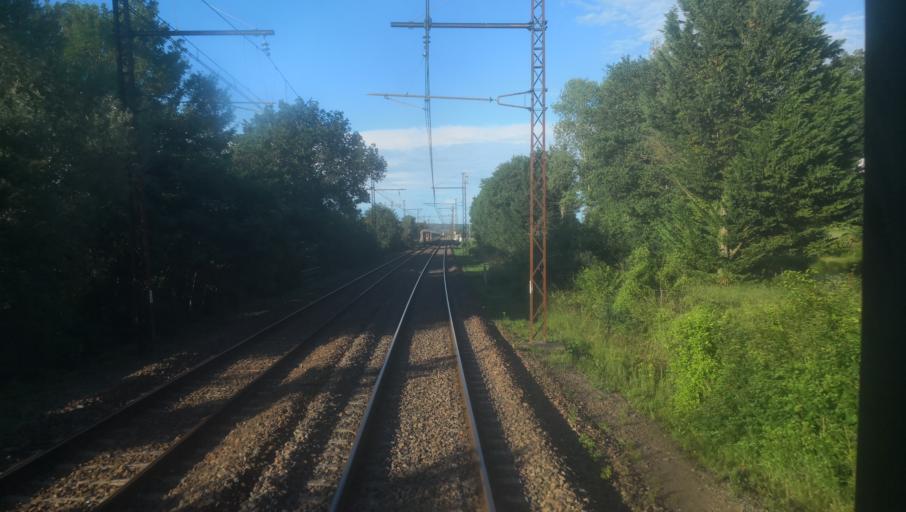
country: FR
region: Centre
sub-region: Departement du Cher
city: Vierzon
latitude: 47.1923
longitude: 2.0782
